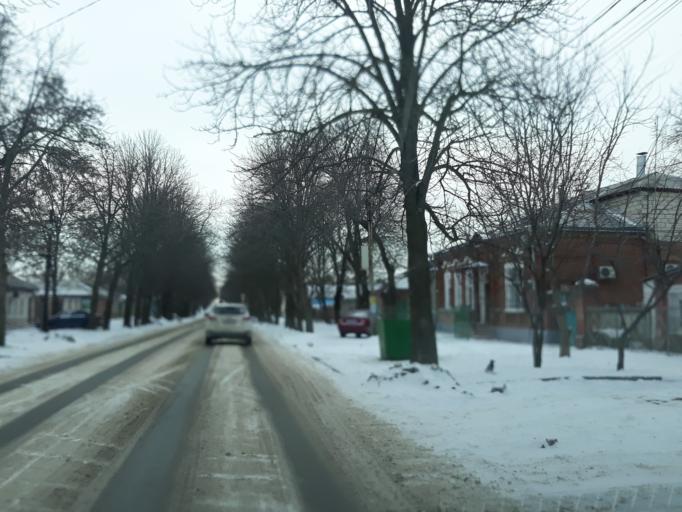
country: RU
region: Rostov
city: Taganrog
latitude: 47.2074
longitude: 38.9219
